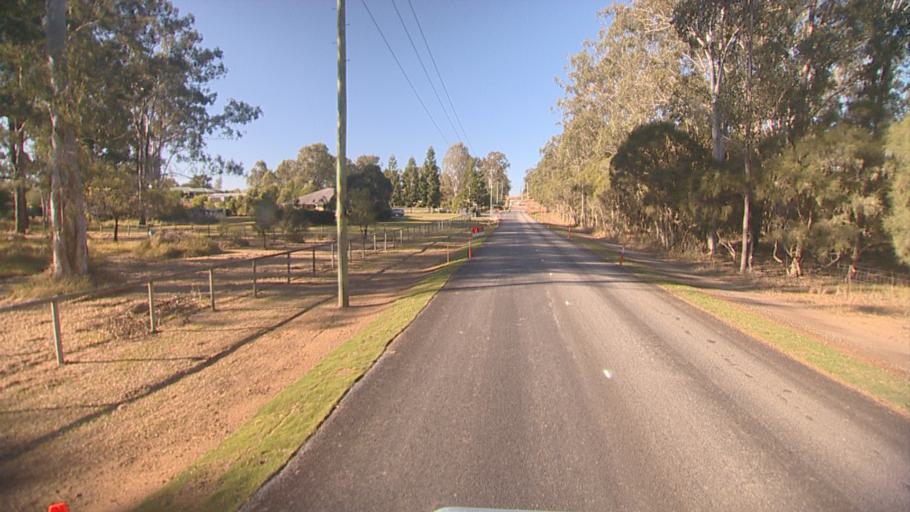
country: AU
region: Queensland
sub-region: Logan
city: Cedar Vale
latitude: -27.8338
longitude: 152.9996
